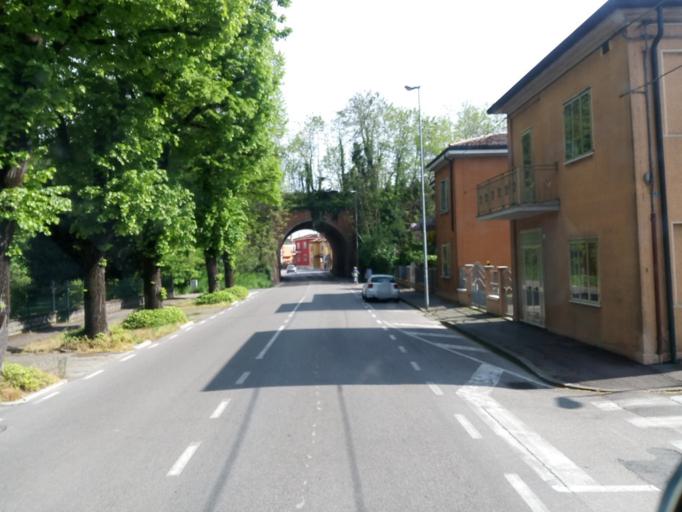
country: IT
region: Veneto
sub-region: Provincia di Verona
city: Boschi Sant'Anna
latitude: 45.1932
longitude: 11.3187
